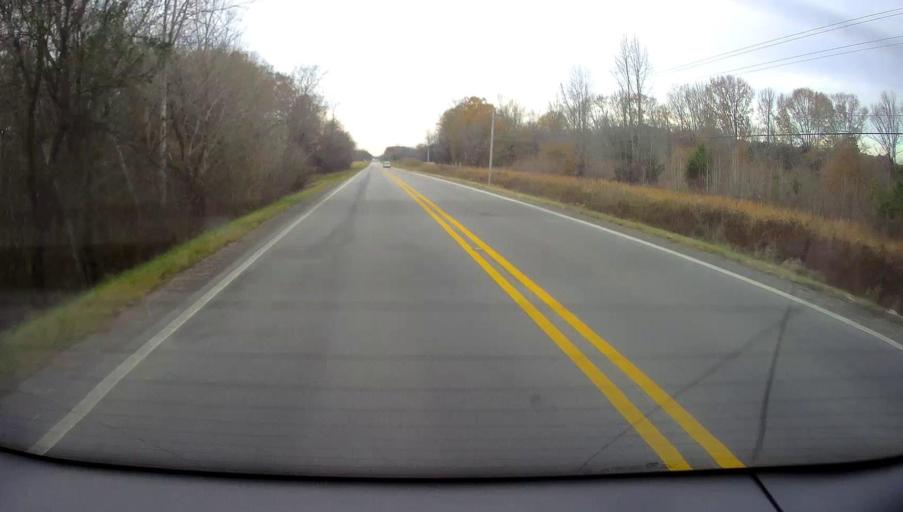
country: US
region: Alabama
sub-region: Morgan County
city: Falkville
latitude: 34.4222
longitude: -86.7156
